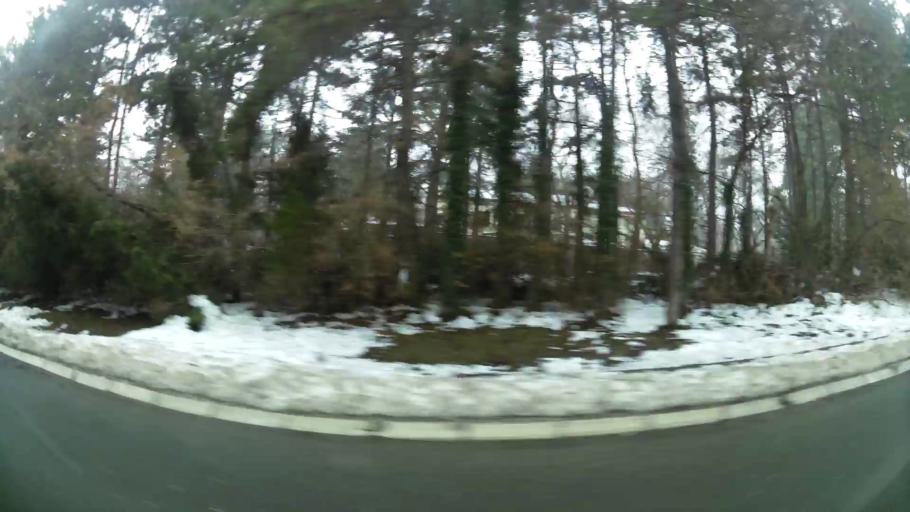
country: RS
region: Central Serbia
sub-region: Belgrade
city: Savski Venac
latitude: 44.7882
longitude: 20.4467
